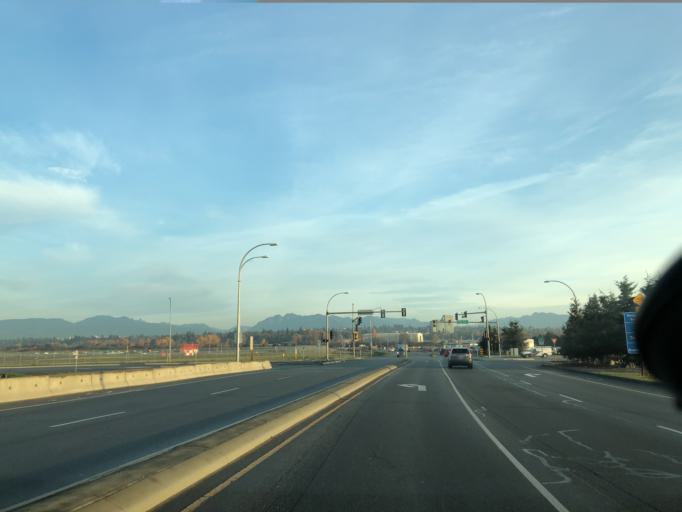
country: CA
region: British Columbia
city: Richmond
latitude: 49.1958
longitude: -123.1507
